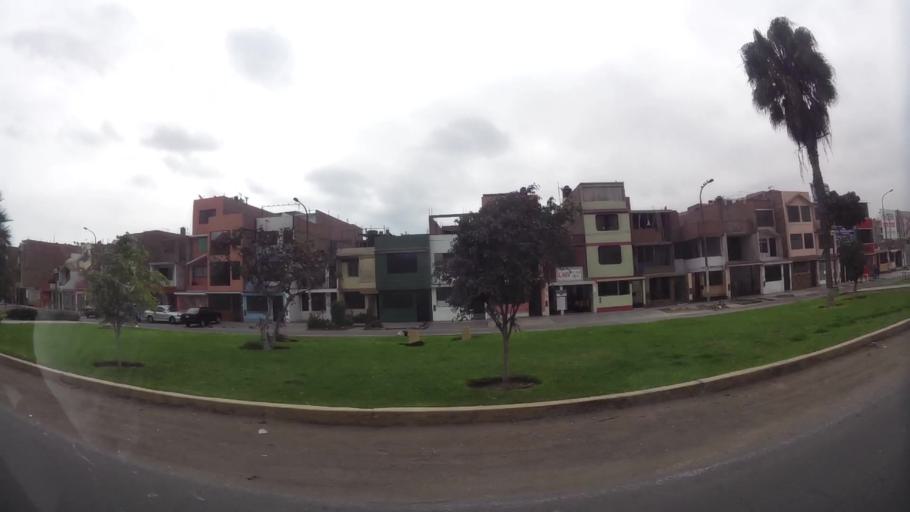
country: PE
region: Callao
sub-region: Callao
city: Callao
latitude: -11.9983
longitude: -77.1158
